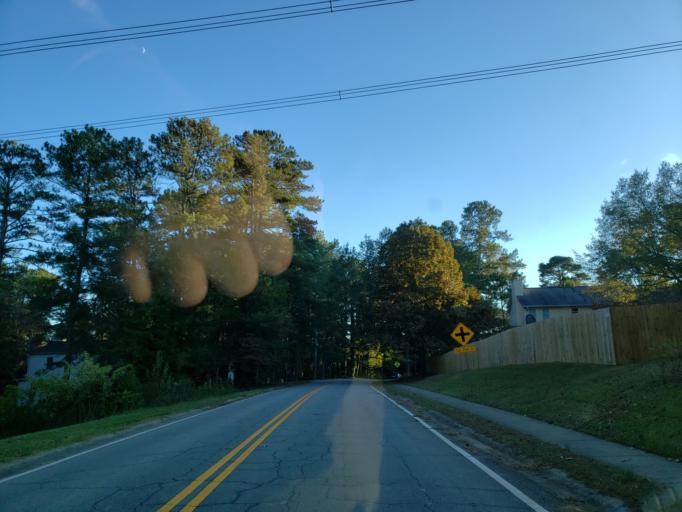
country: US
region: Georgia
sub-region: Fulton County
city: Roswell
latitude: 33.9918
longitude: -84.4357
